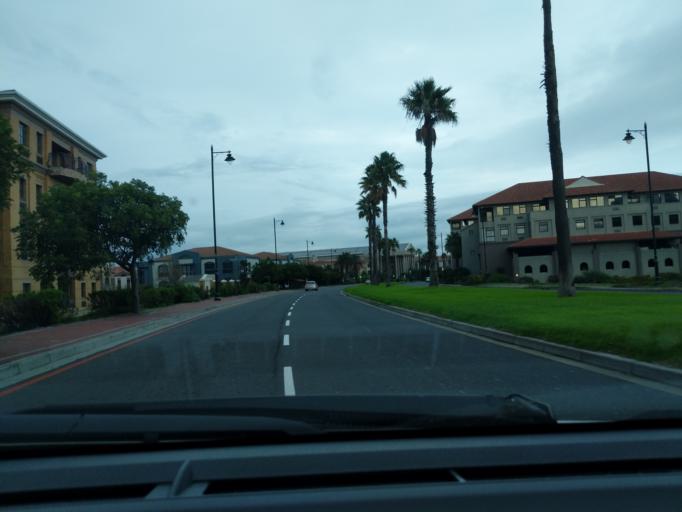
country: ZA
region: Western Cape
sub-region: City of Cape Town
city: Sunset Beach
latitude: -33.8877
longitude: 18.5202
